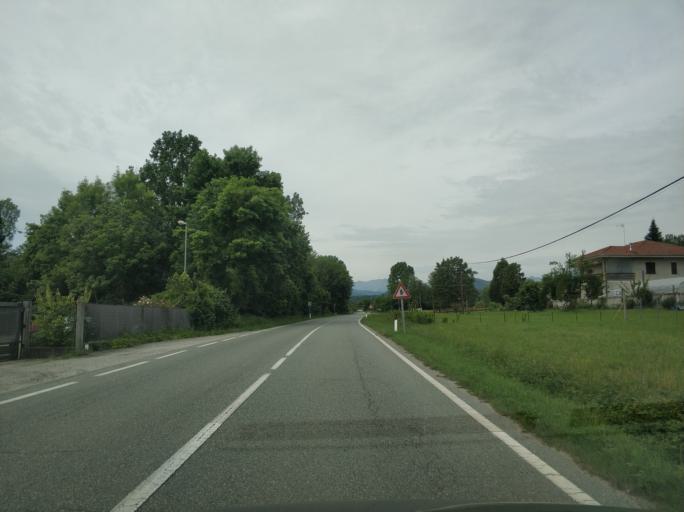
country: IT
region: Piedmont
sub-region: Provincia di Torino
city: Levone
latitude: 45.3185
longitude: 7.6166
